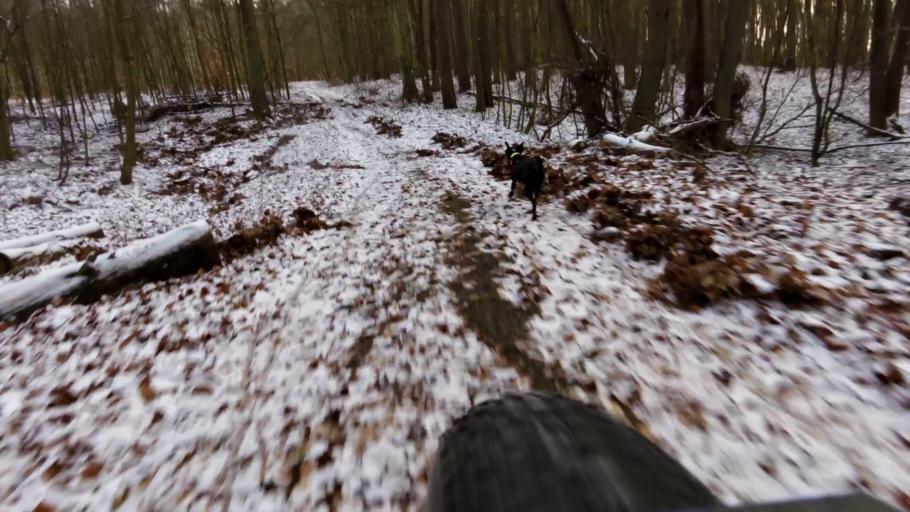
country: PL
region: West Pomeranian Voivodeship
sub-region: Powiat walecki
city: Tuczno
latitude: 53.2933
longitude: 16.2939
